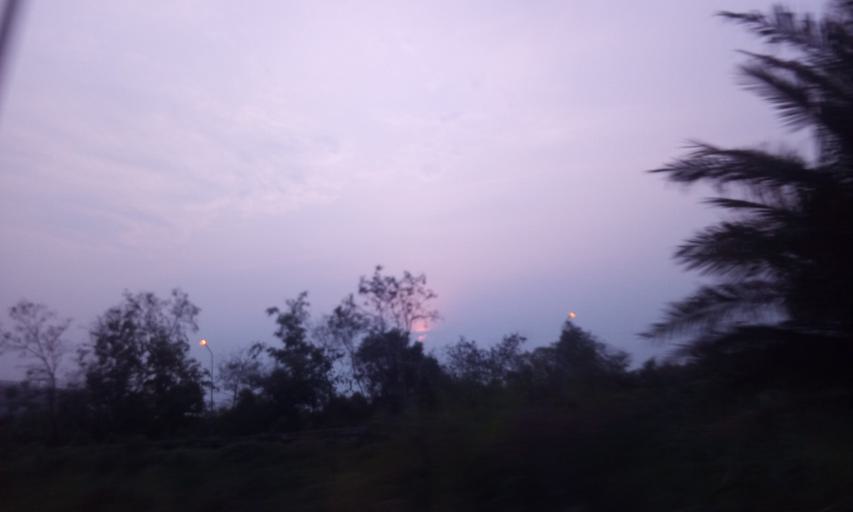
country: TH
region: Pathum Thani
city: Ban Lam Luk Ka
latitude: 14.0205
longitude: 100.8942
